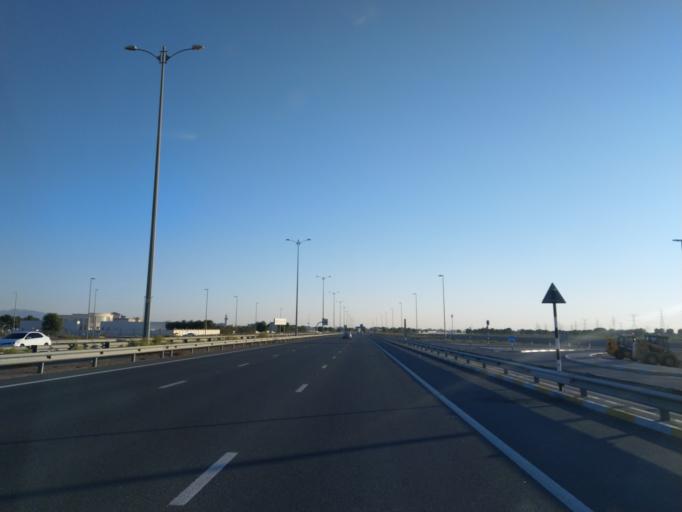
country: OM
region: Al Buraimi
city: Al Buraymi
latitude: 24.2889
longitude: 55.7352
